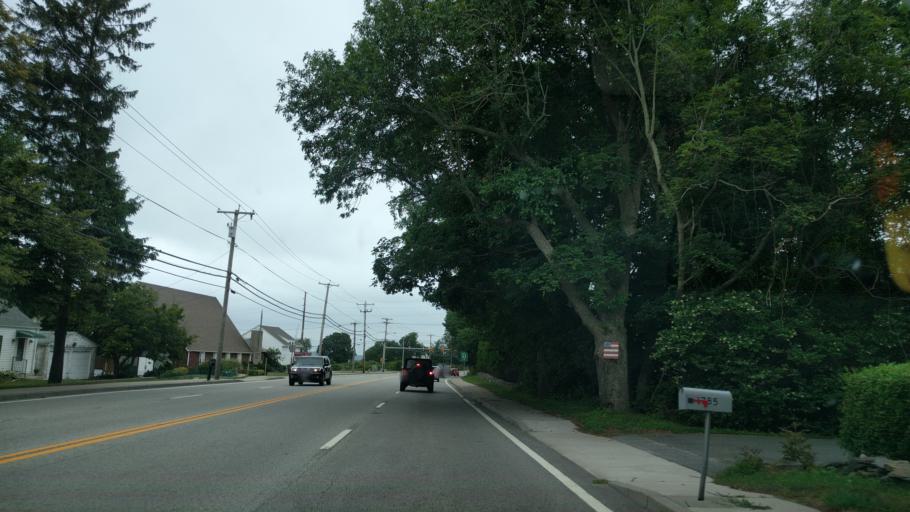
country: US
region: Rhode Island
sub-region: Newport County
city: Middletown
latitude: 41.5468
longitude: -71.2919
